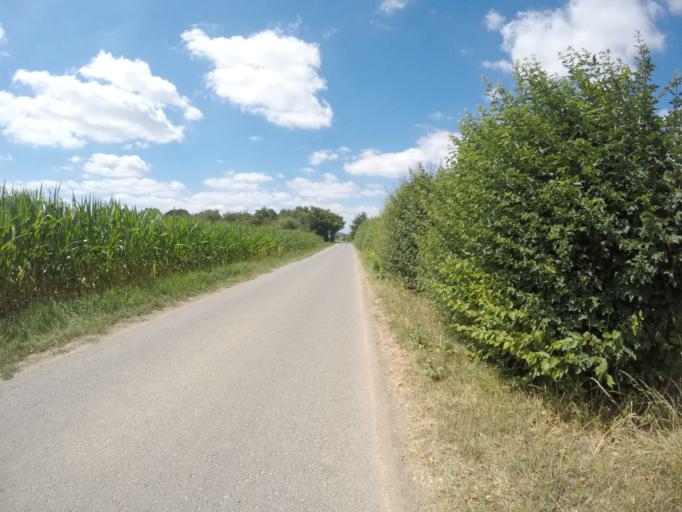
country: DE
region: Lower Saxony
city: Rinteln
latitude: 52.1825
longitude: 9.0196
